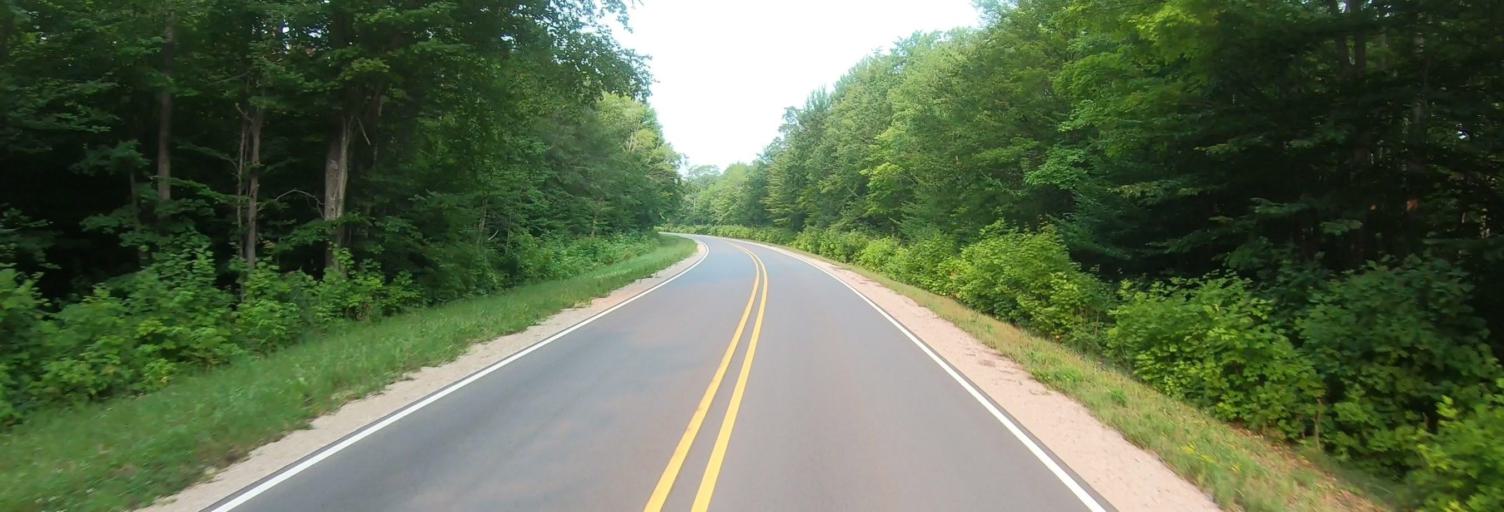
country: US
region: Michigan
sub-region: Luce County
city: Newberry
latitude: 46.4859
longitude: -85.0469
